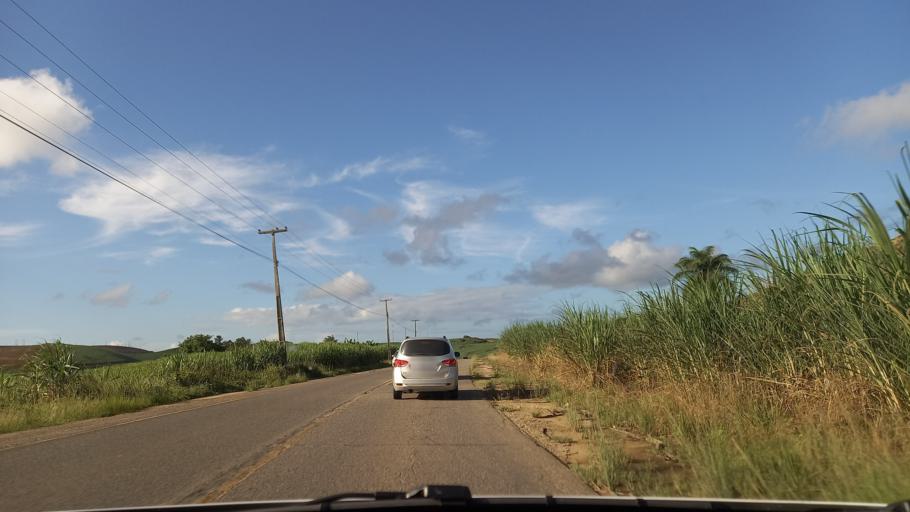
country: BR
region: Pernambuco
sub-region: Sirinhaem
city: Sirinhaem
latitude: -8.6108
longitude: -35.1192
